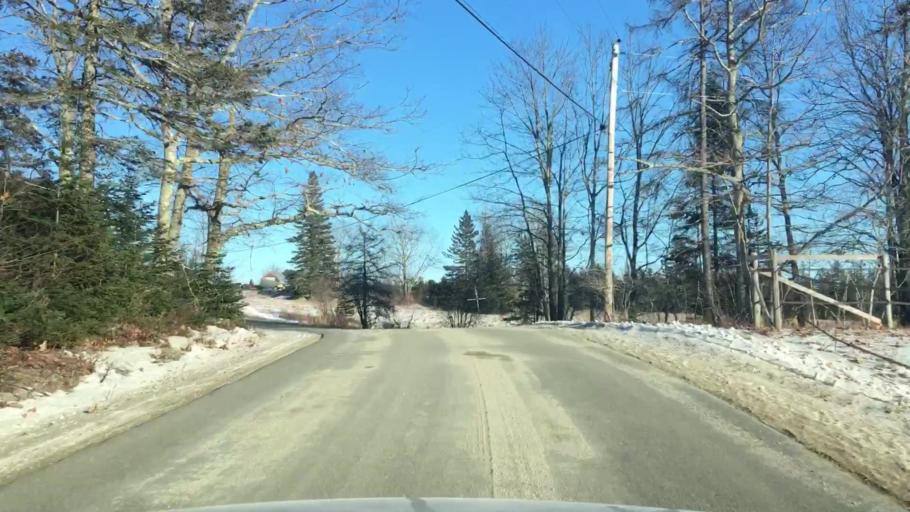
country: US
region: Maine
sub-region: Hancock County
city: Castine
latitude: 44.3821
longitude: -68.7265
